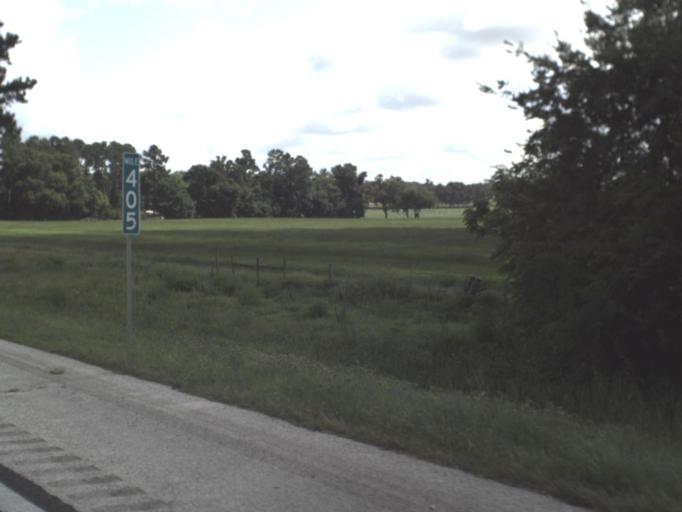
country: US
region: Florida
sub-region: Alachua County
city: High Springs
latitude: 29.8838
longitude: -82.5440
